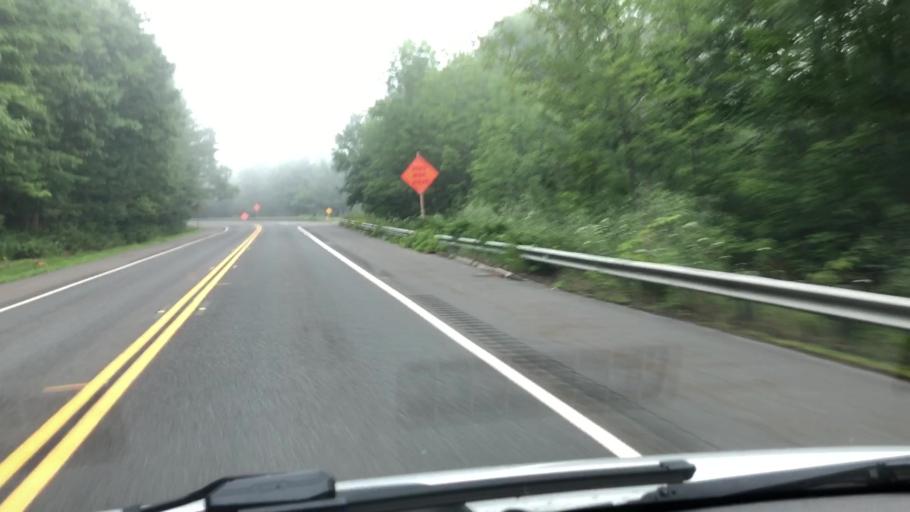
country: US
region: Massachusetts
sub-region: Hampshire County
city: Chesterfield
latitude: 42.4899
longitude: -72.9679
